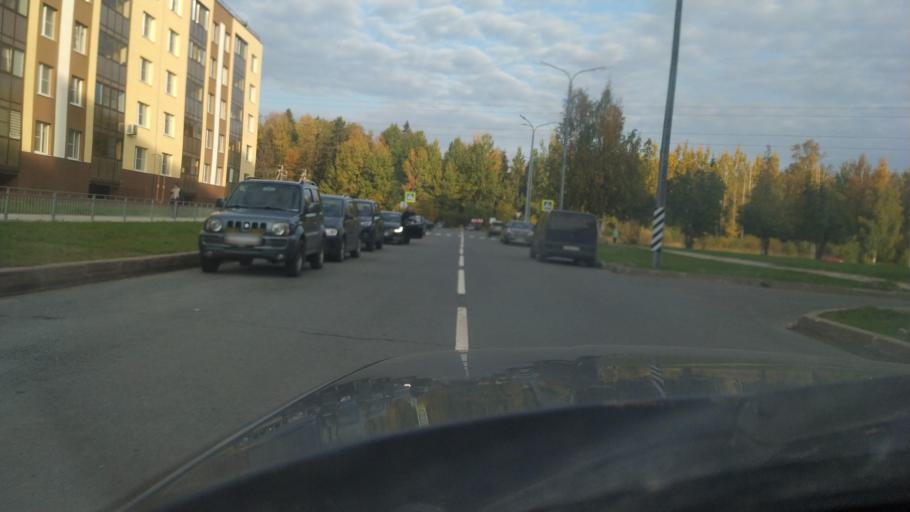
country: RU
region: Leningrad
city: Sosnovyy Bor
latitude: 59.9170
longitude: 29.0831
